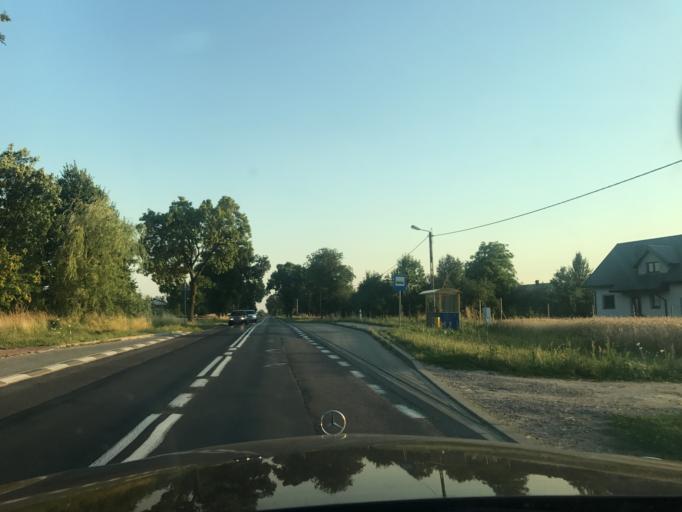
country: PL
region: Lublin Voivodeship
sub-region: Powiat lubartowski
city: Lubartow
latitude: 51.4962
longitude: 22.6369
